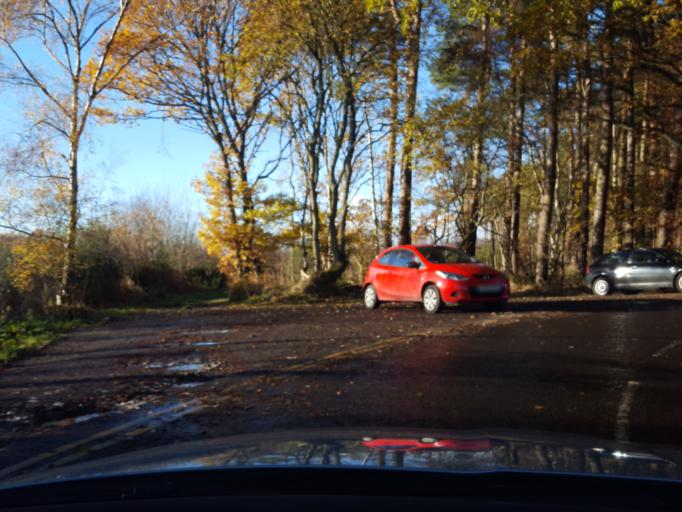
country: GB
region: Scotland
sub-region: Perth and Kinross
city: Scone
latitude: 56.4238
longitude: -3.4149
